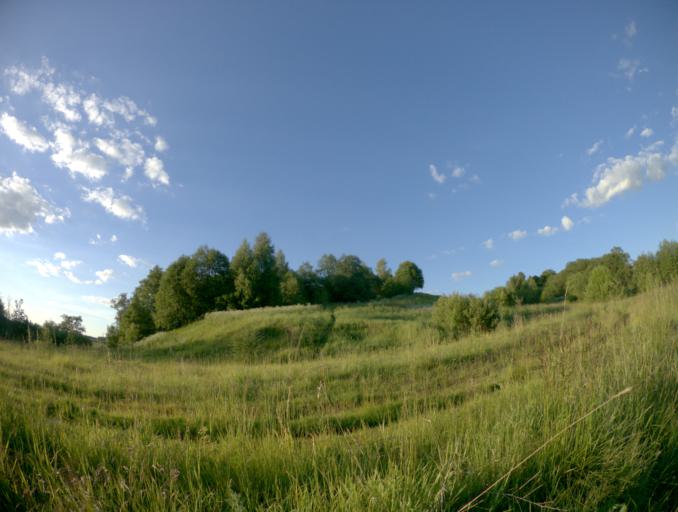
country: RU
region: Vladimir
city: Stavrovo
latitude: 56.2955
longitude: 39.9450
